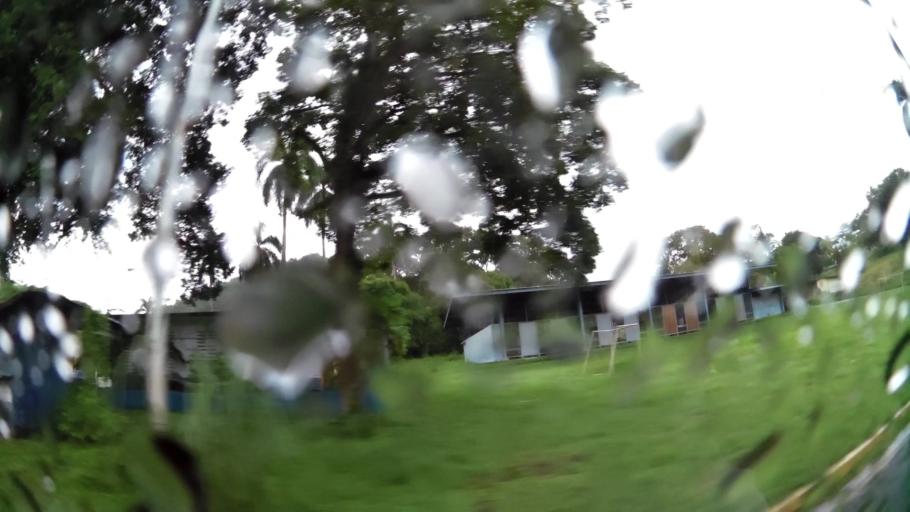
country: PA
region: Panama
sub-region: Distrito de Panama
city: Paraiso
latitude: 9.0201
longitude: -79.6102
